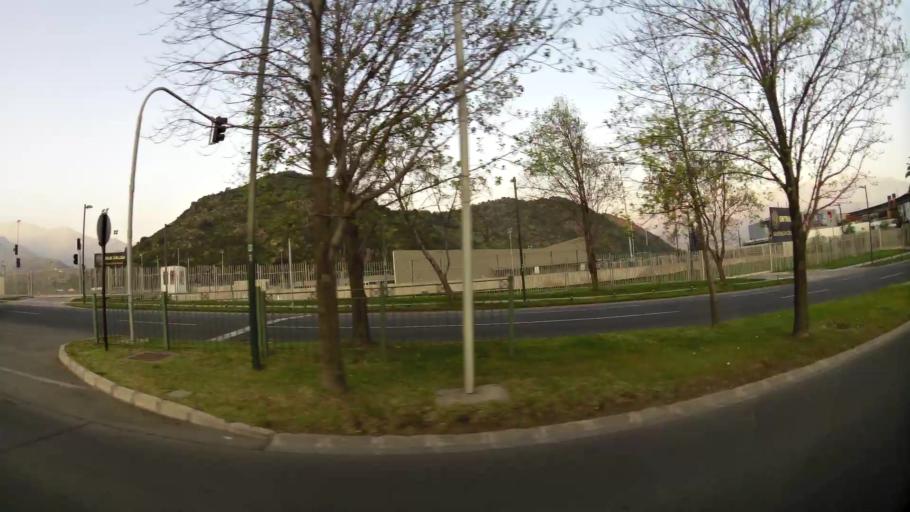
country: CL
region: Santiago Metropolitan
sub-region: Provincia de Chacabuco
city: Chicureo Abajo
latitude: -33.3415
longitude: -70.5460
